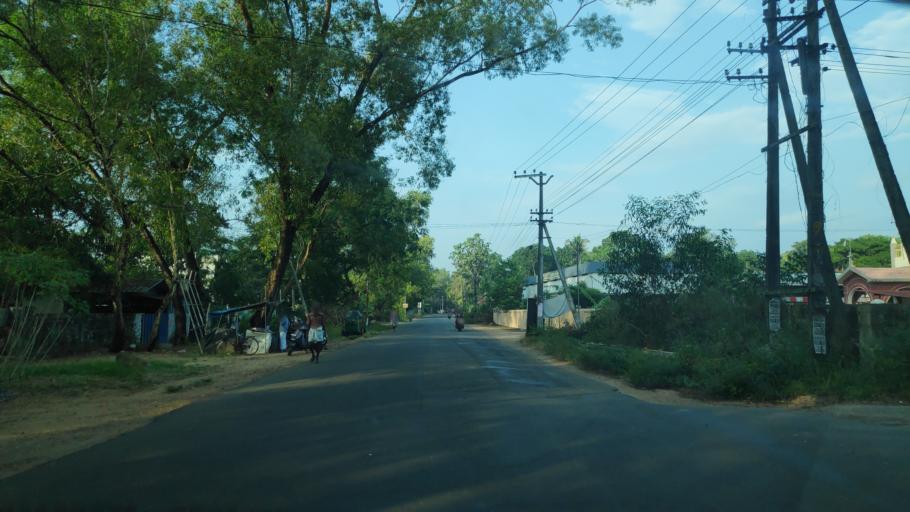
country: IN
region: Kerala
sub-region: Alappuzha
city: Shertallai
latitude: 9.6107
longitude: 76.3619
